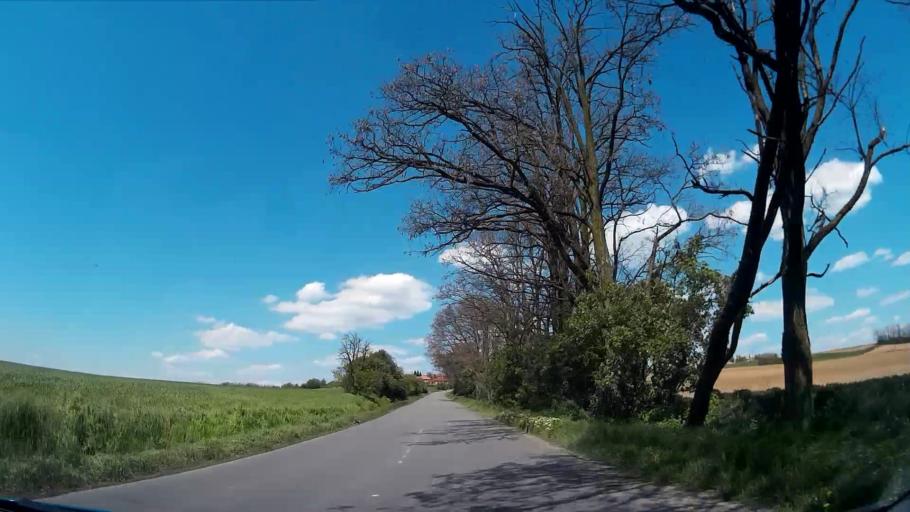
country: CZ
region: South Moravian
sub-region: Okres Brno-Venkov
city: Rosice
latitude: 49.1506
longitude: 16.3821
